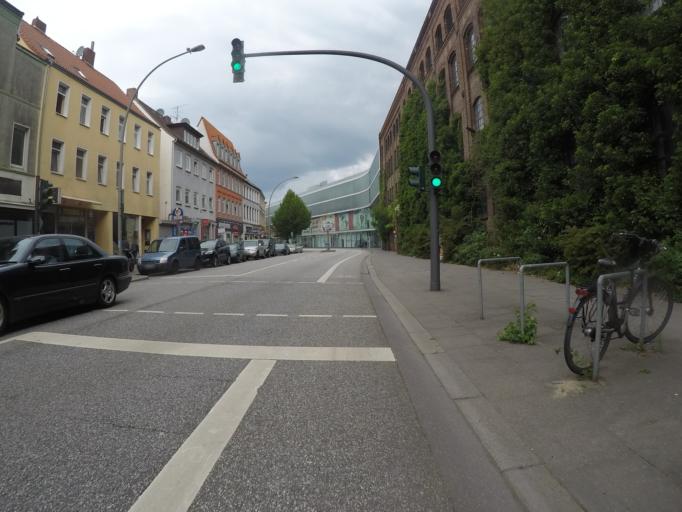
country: DE
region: Hamburg
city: Harburg
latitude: 53.4548
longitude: 9.9876
